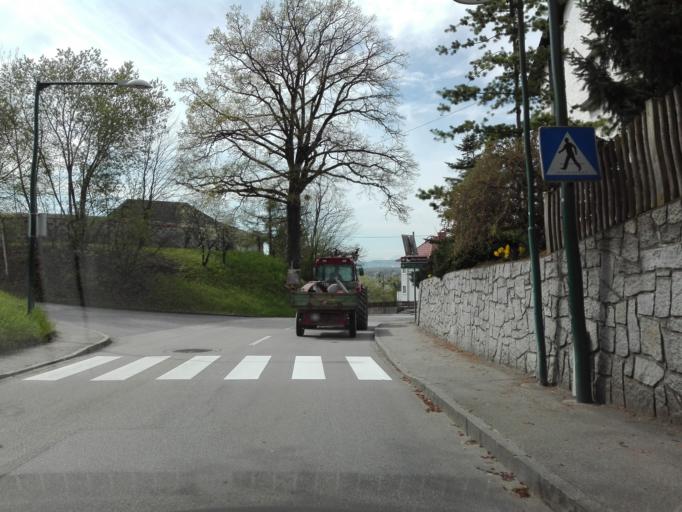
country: AT
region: Upper Austria
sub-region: Politischer Bezirk Urfahr-Umgebung
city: Walding
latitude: 48.3535
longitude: 14.1598
